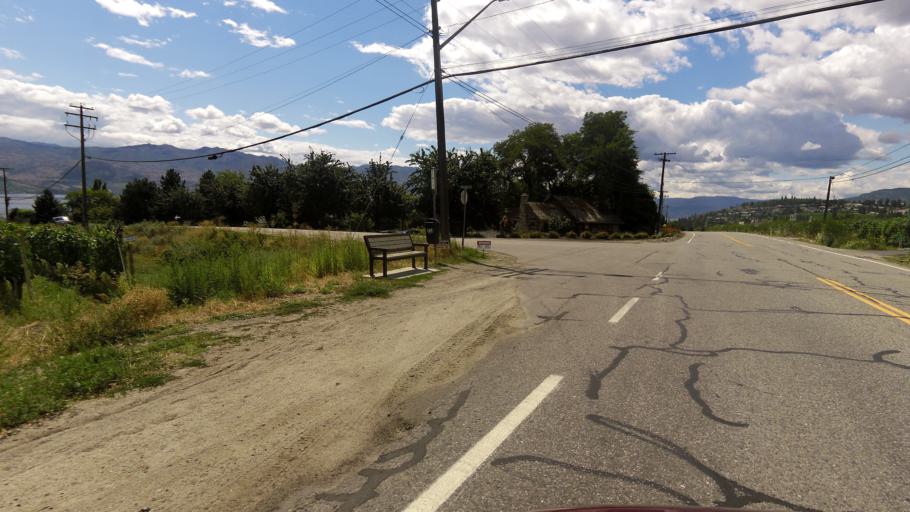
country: CA
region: British Columbia
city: West Kelowna
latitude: 49.8439
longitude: -119.5654
